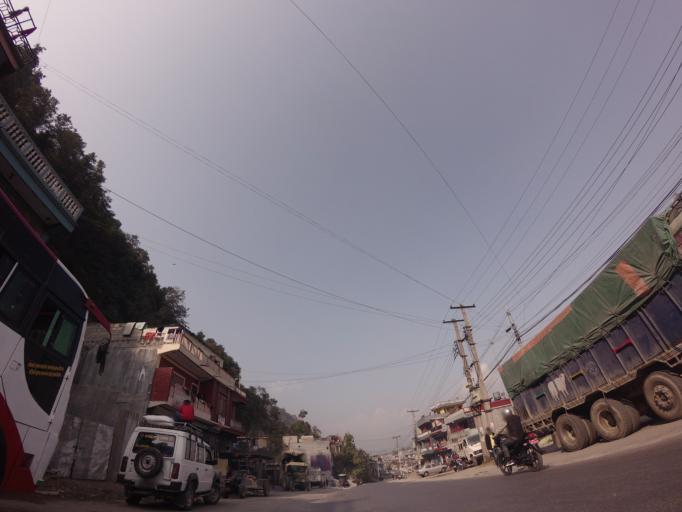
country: NP
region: Western Region
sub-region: Gandaki Zone
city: Pokhara
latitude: 28.2438
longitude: 83.9829
